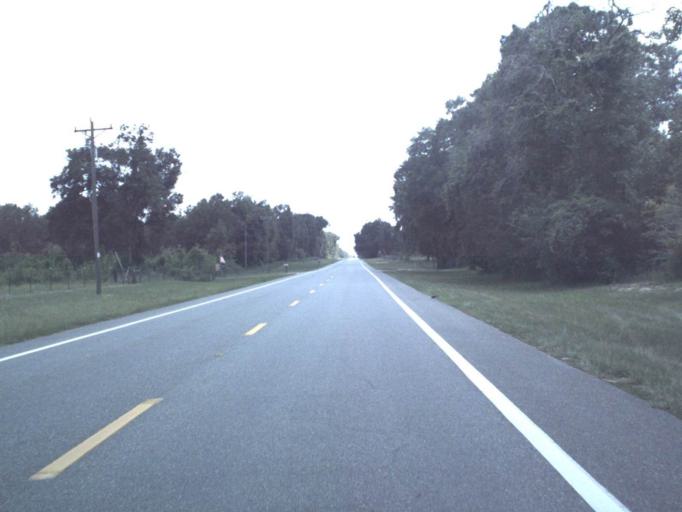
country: US
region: Florida
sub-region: Alachua County
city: High Springs
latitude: 29.7945
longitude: -82.7411
